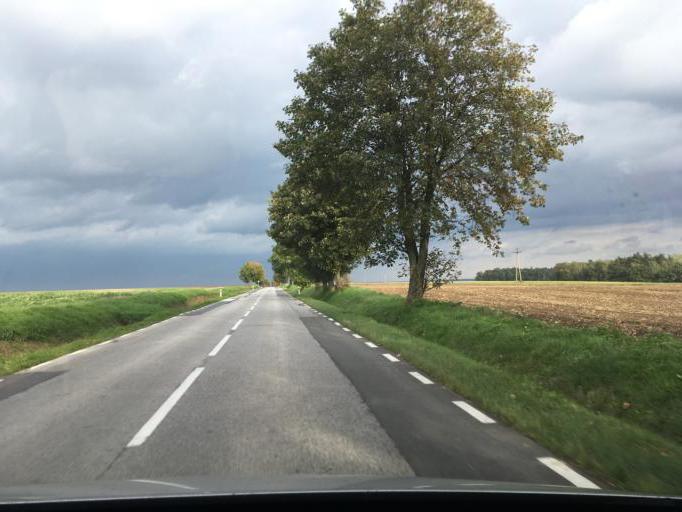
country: PL
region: Swietokrzyskie
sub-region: Powiat pinczowski
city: Michalow
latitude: 50.4704
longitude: 20.4195
